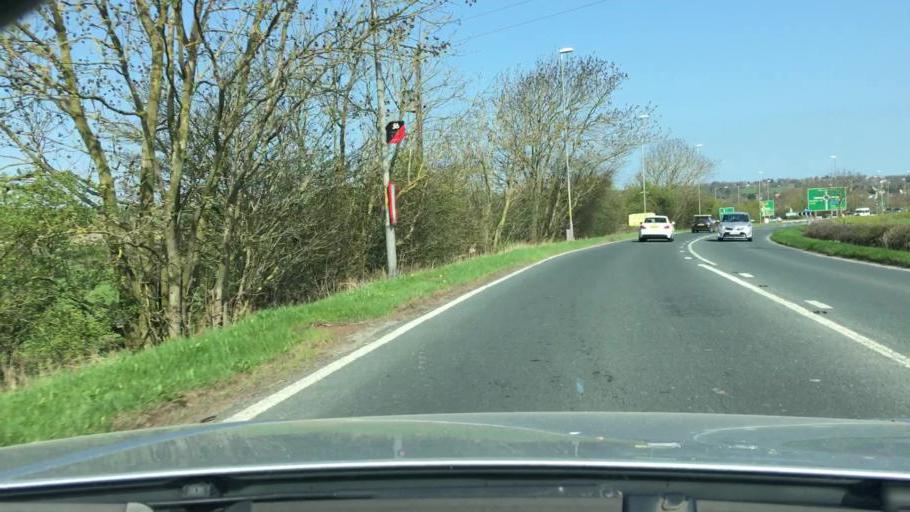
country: GB
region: England
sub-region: North Yorkshire
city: Pannal
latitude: 53.9458
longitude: -1.5403
